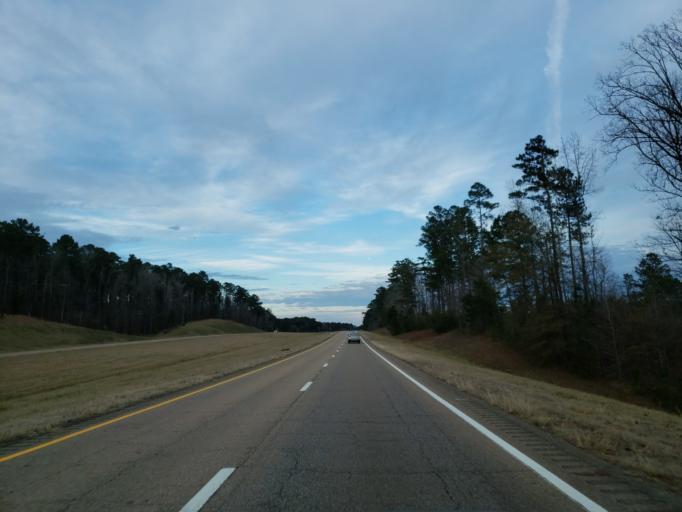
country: US
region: Mississippi
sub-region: Lauderdale County
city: Meridian Station
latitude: 32.4828
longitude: -88.5948
